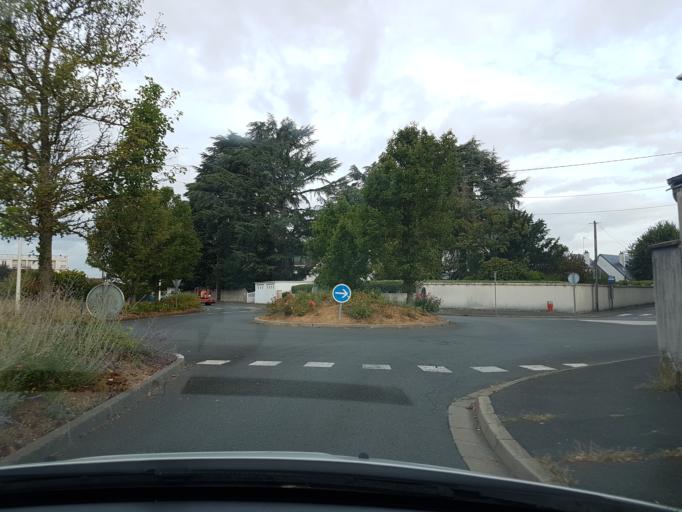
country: FR
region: Centre
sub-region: Departement d'Indre-et-Loire
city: Joue-les-Tours
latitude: 47.3562
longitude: 0.6919
